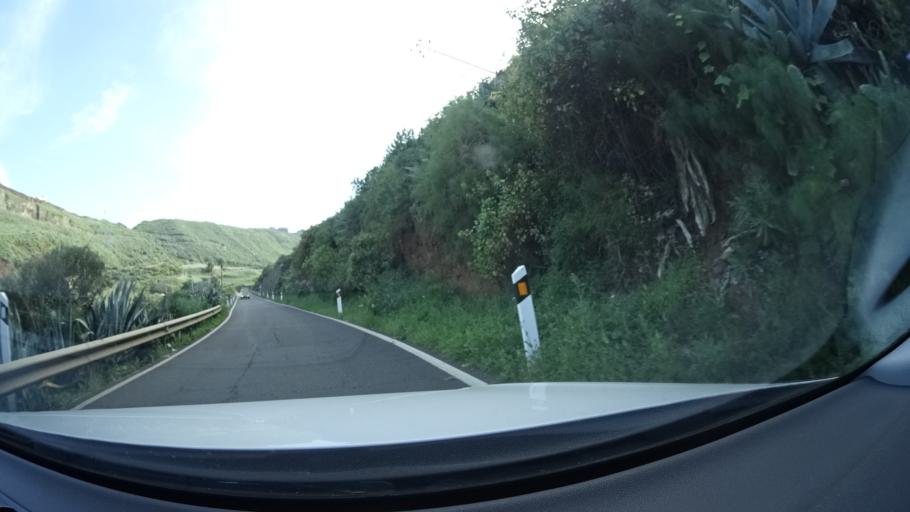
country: ES
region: Canary Islands
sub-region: Provincia de Las Palmas
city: Guia
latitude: 28.1102
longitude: -15.6417
